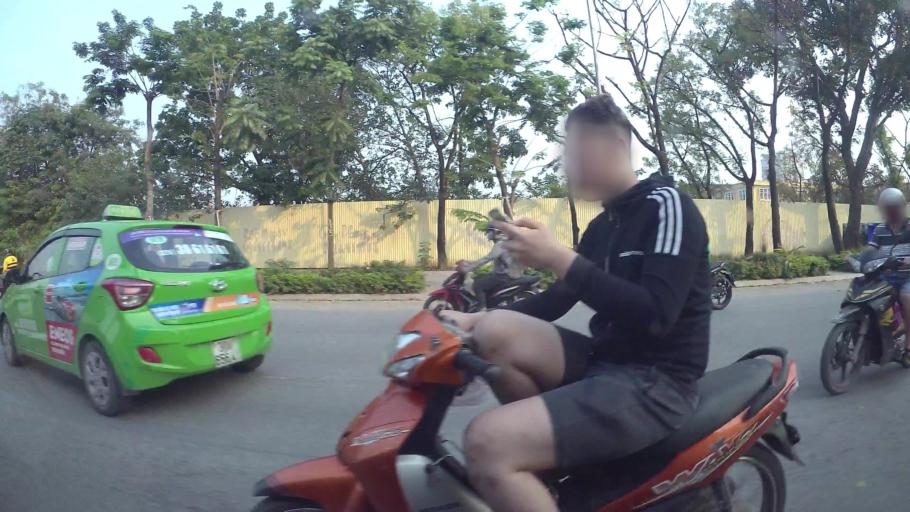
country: VN
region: Ha Noi
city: Thanh Xuan
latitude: 20.9961
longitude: 105.8103
